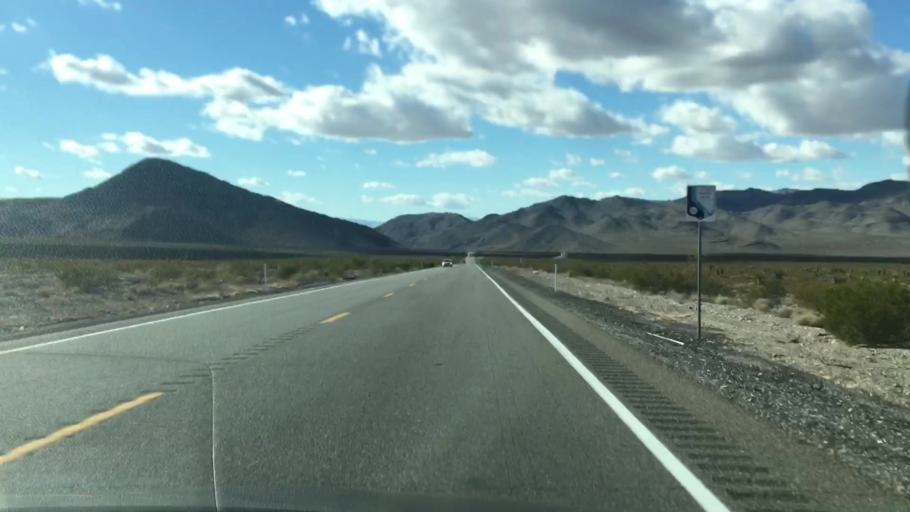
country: US
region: Nevada
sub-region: Nye County
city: Pahrump
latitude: 36.5929
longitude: -116.0260
